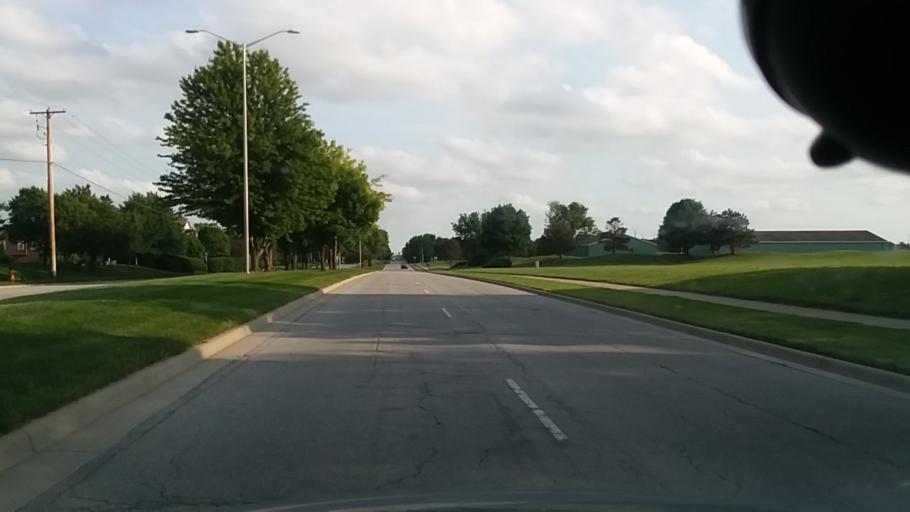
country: US
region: Kansas
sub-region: Johnson County
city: Olathe
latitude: 38.9541
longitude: -94.8162
